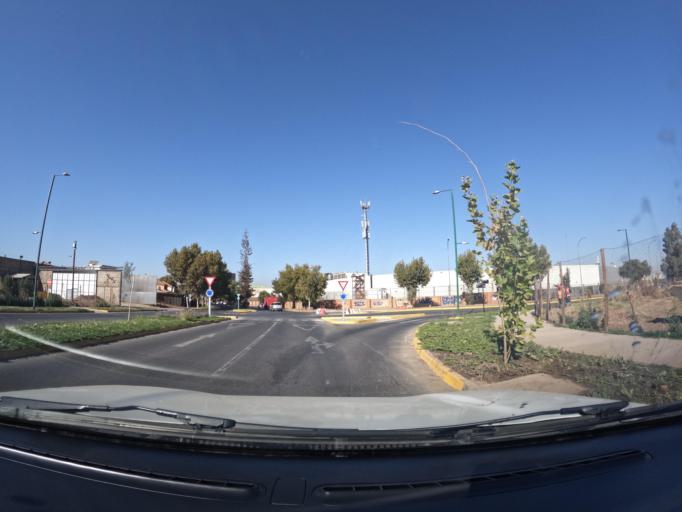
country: CL
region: Santiago Metropolitan
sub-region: Provincia de Santiago
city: Villa Presidente Frei, Nunoa, Santiago, Chile
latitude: -33.4851
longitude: -70.5768
